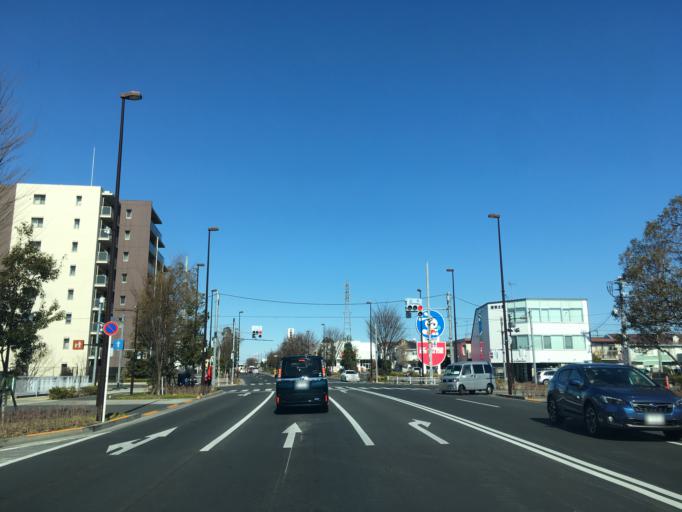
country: JP
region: Tokyo
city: Mitaka-shi
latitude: 35.6887
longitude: 139.5505
